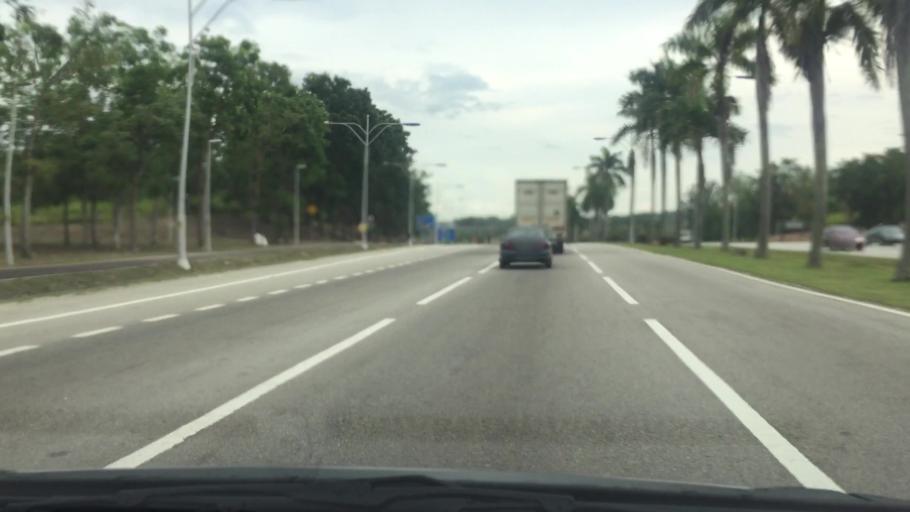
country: MY
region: Putrajaya
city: Putrajaya
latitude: 2.8997
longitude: 101.6581
